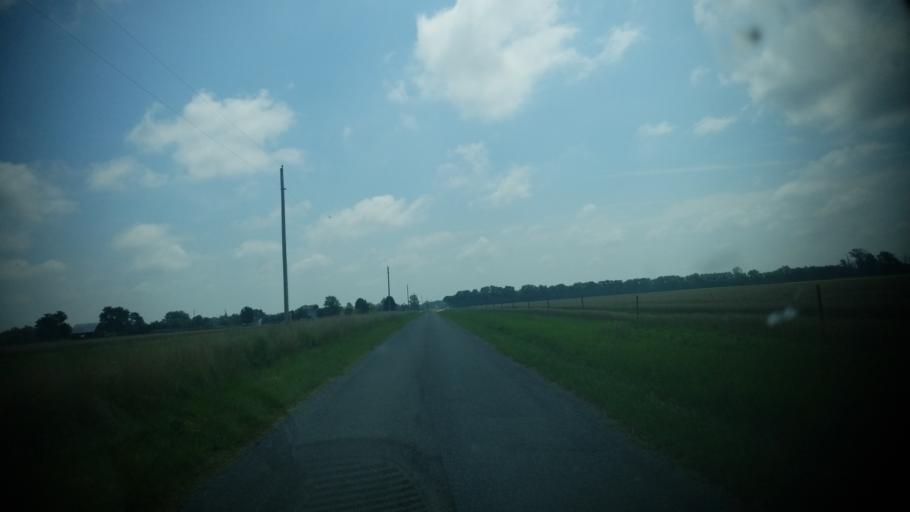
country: US
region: Illinois
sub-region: Wayne County
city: Fairfield
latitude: 38.5300
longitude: -88.3876
